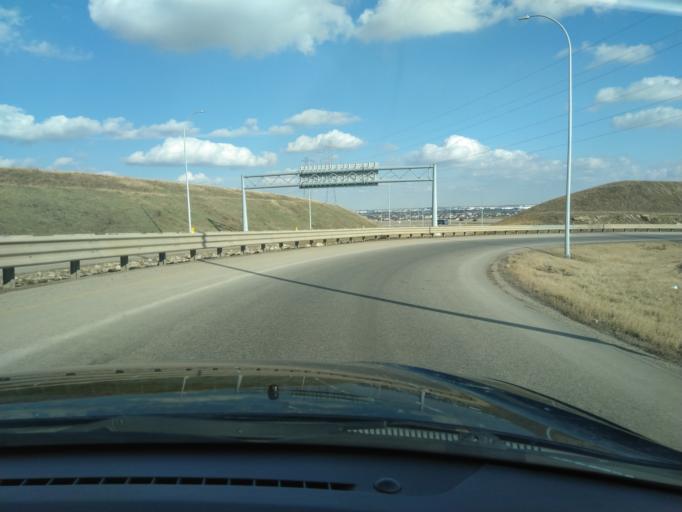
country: CA
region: Alberta
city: Calgary
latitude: 51.1749
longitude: -114.0677
